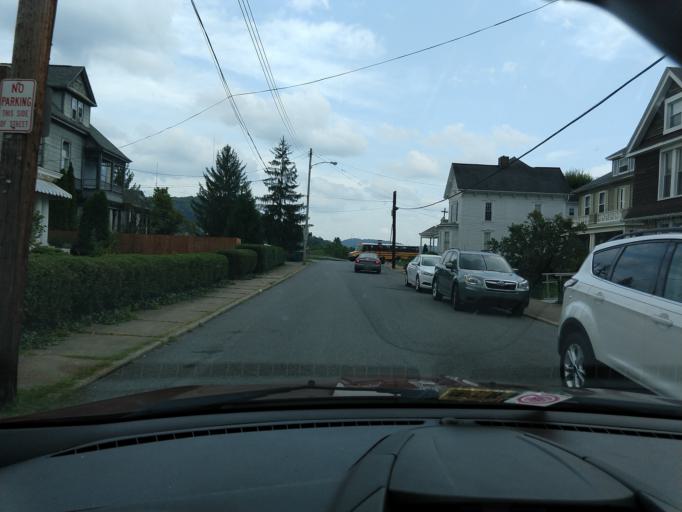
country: US
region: West Virginia
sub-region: Harrison County
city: Clarksburg
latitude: 39.2823
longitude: -80.3403
